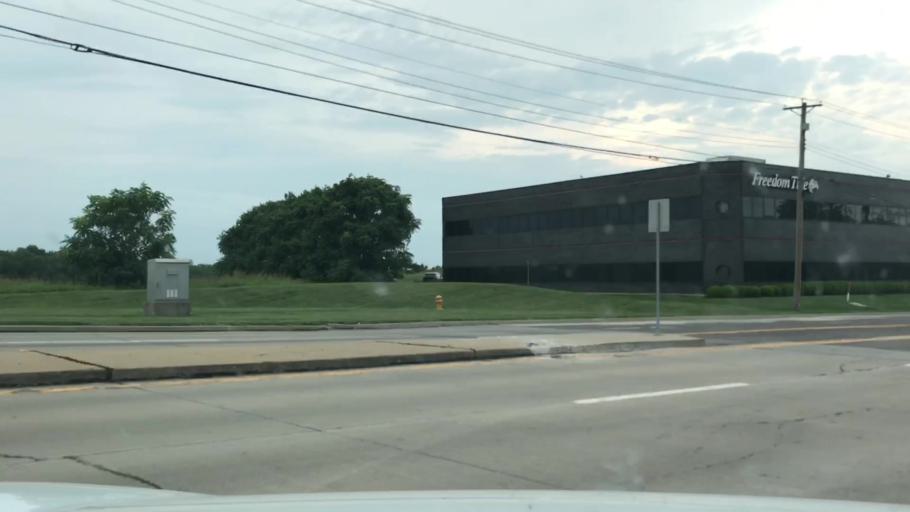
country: US
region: Missouri
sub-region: Saint Louis County
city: Chesterfield
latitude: 38.6595
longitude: -90.5694
